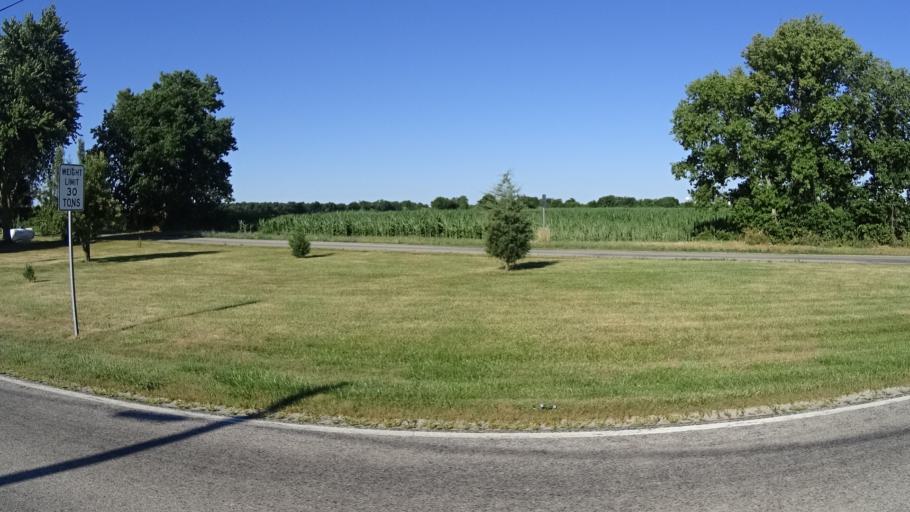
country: US
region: Ohio
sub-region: Erie County
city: Sandusky
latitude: 41.3778
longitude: -82.7699
